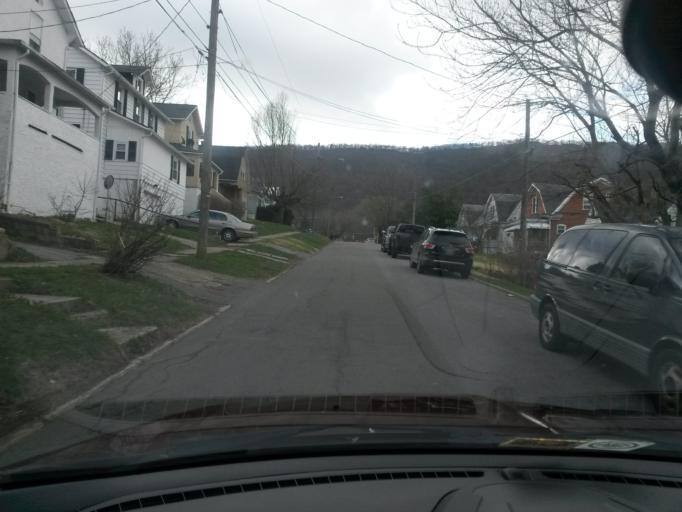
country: US
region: West Virginia
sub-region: Mercer County
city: Bluefield
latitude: 37.2519
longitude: -81.2154
